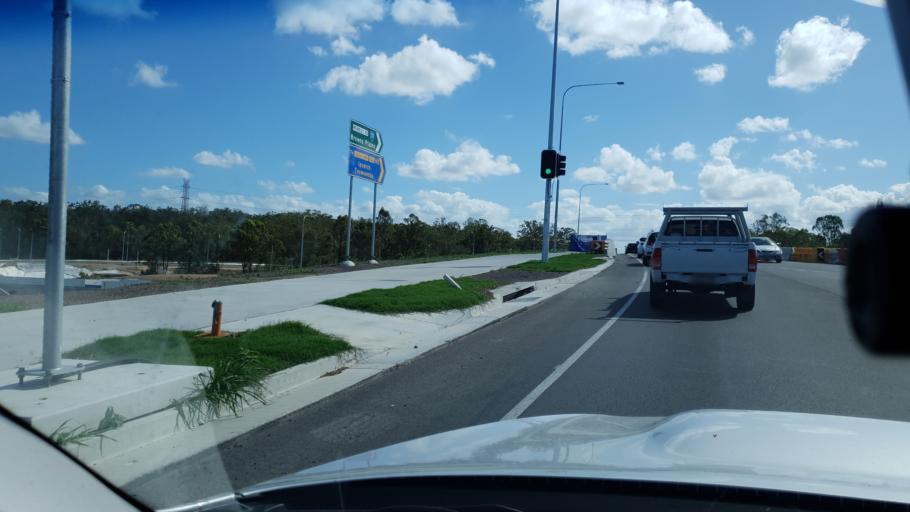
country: AU
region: Queensland
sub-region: Logan
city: Woodridge
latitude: -27.6517
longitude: 153.0711
